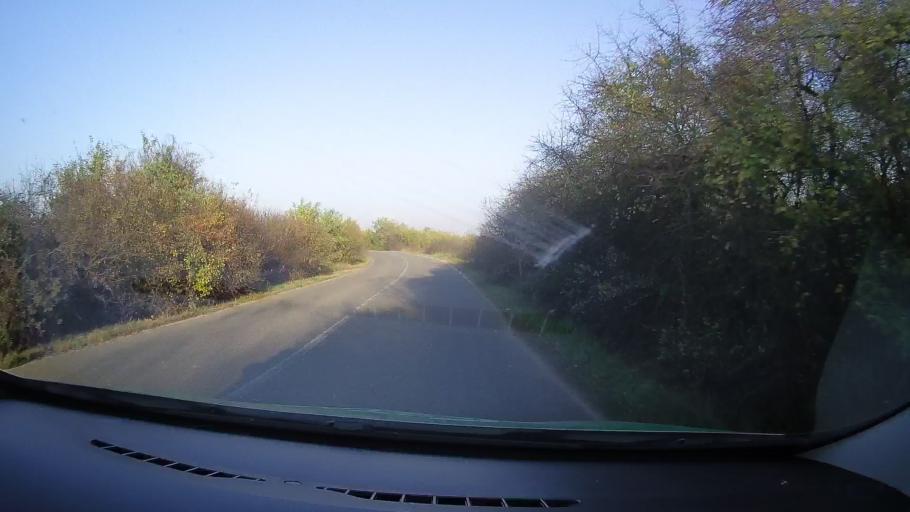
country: RO
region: Arad
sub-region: Comuna Tarnova
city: Chier
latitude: 46.3325
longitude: 21.8673
